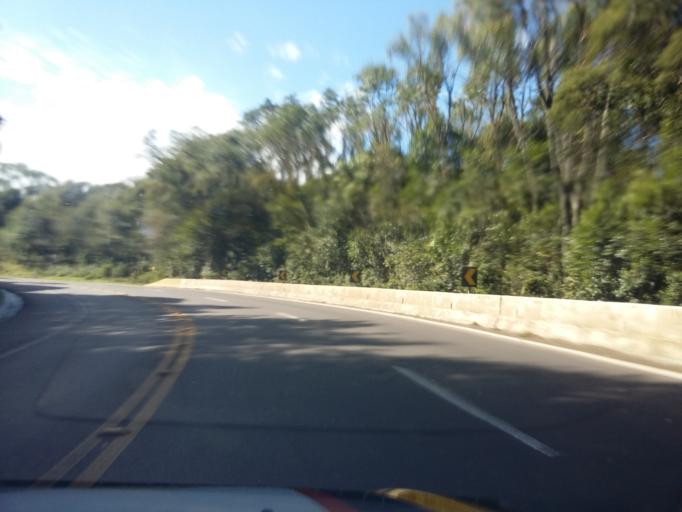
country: BR
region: Rio Grande do Sul
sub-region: Vacaria
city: Vacaria
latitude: -28.5827
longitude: -51.0244
